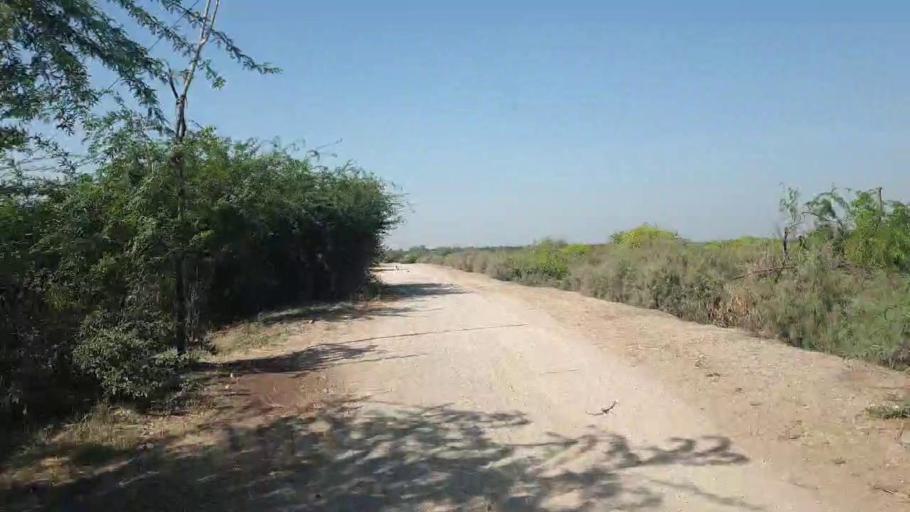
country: PK
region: Sindh
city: Talhar
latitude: 24.8289
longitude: 68.7794
